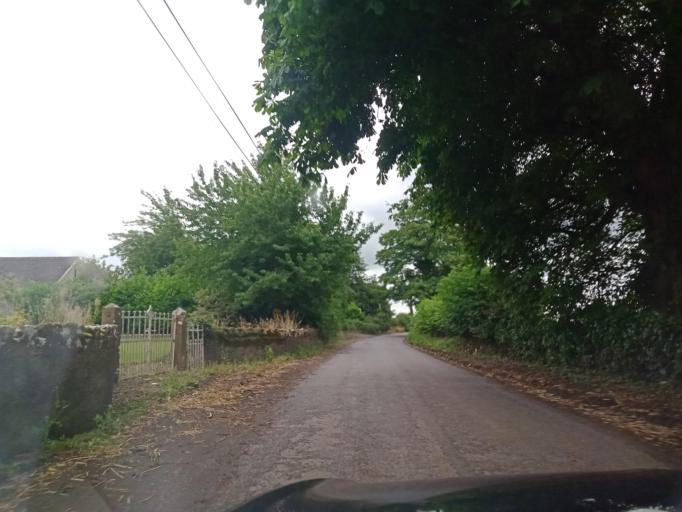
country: IE
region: Leinster
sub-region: Laois
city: Stradbally
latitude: 52.9809
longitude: -7.1644
